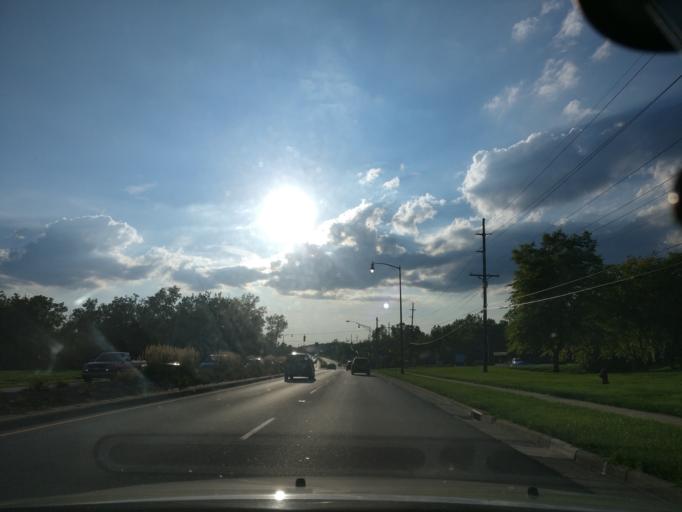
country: US
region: Ohio
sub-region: Warren County
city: Springboro
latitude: 39.5605
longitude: -84.2460
